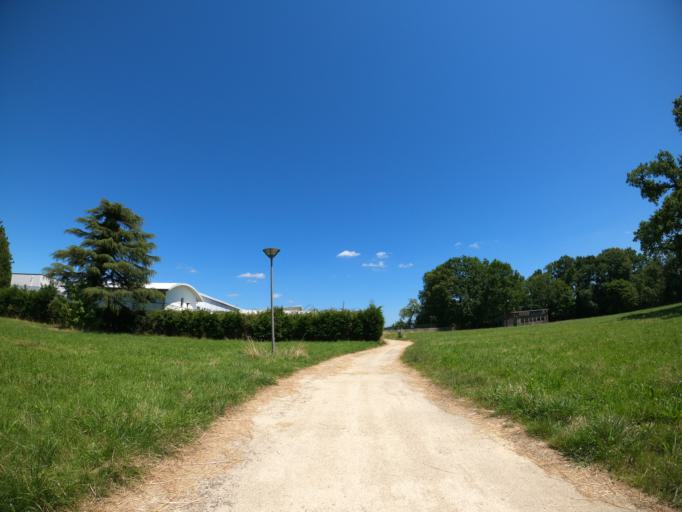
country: FR
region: Aquitaine
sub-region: Departement des Pyrenees-Atlantiques
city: Boucau
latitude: 43.5268
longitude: -1.4516
